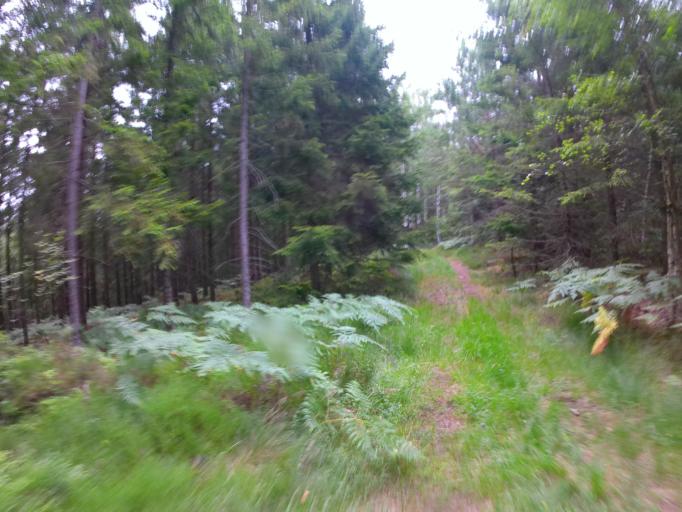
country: SE
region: Vaestra Goetaland
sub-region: Alingsas Kommun
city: Alingsas
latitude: 58.0223
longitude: 12.5536
